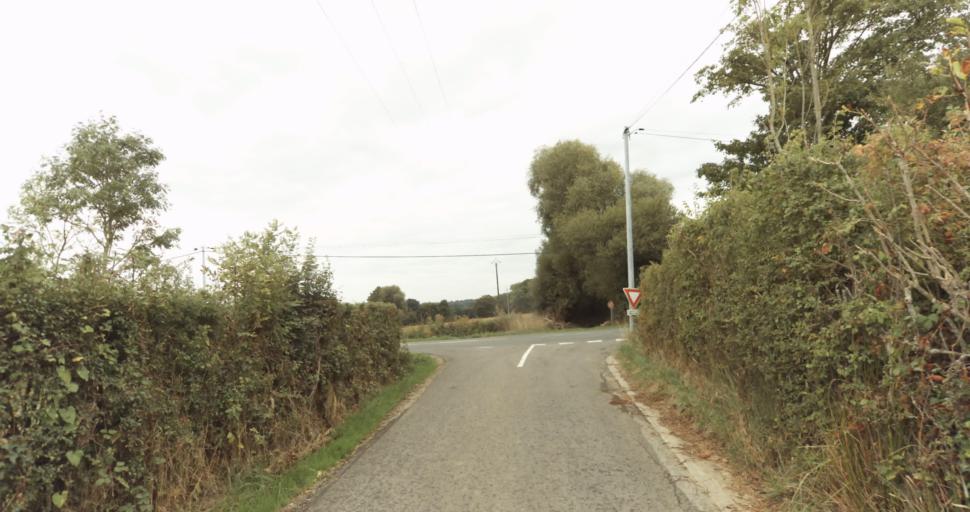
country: FR
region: Lower Normandy
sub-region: Departement de l'Orne
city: Gace
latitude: 48.6899
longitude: 0.2888
